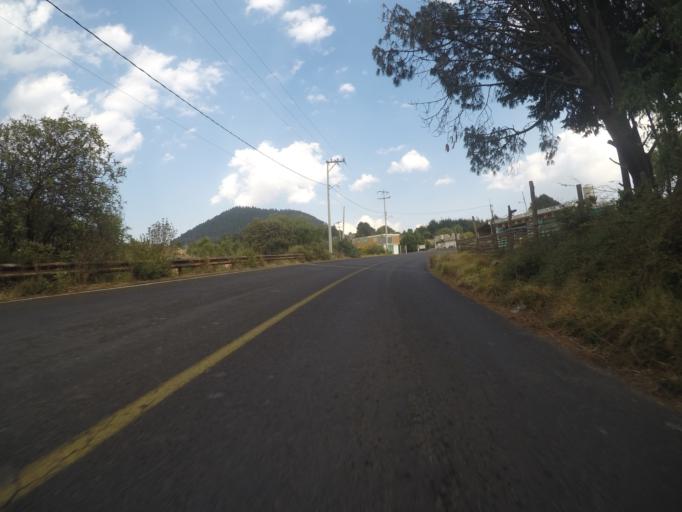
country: MX
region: Mexico
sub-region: Xalatlaco
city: San Juan Tomasquillo Herradura
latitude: 19.1657
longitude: -99.3921
